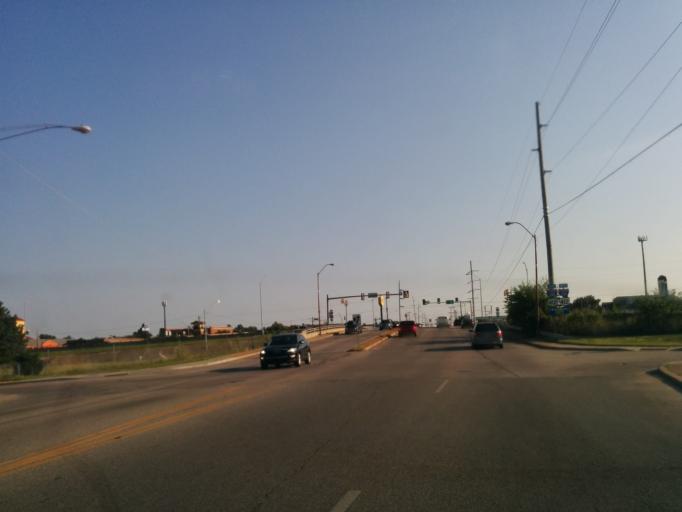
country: US
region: Oklahoma
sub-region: Tulsa County
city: Tulsa
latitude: 36.1644
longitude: -95.9047
